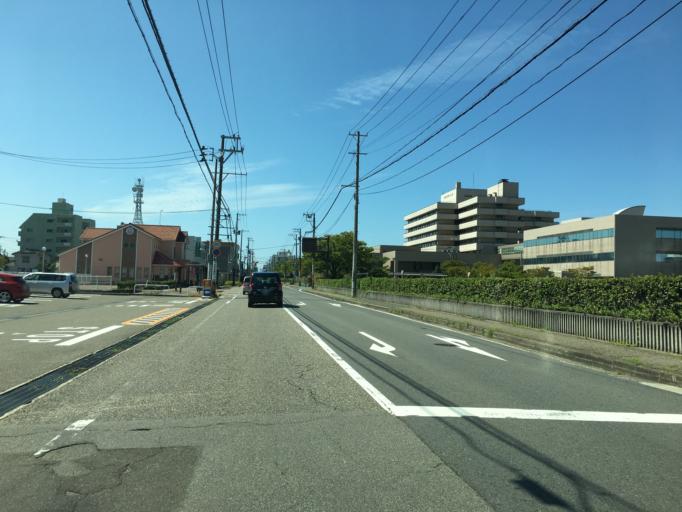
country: JP
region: Niigata
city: Niigata-shi
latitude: 37.9107
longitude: 139.0319
